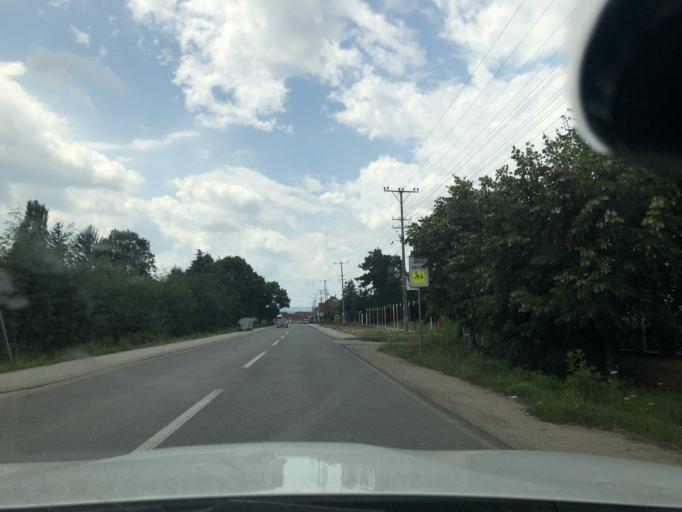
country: RS
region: Central Serbia
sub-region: Jablanicki Okrug
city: Lebane
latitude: 42.9506
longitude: 21.8294
